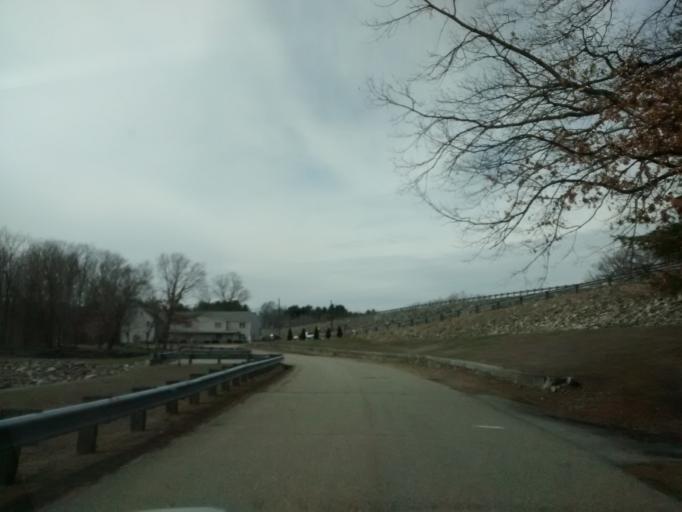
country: US
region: Massachusetts
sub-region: Worcester County
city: Oxford
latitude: 42.1197
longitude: -71.8776
